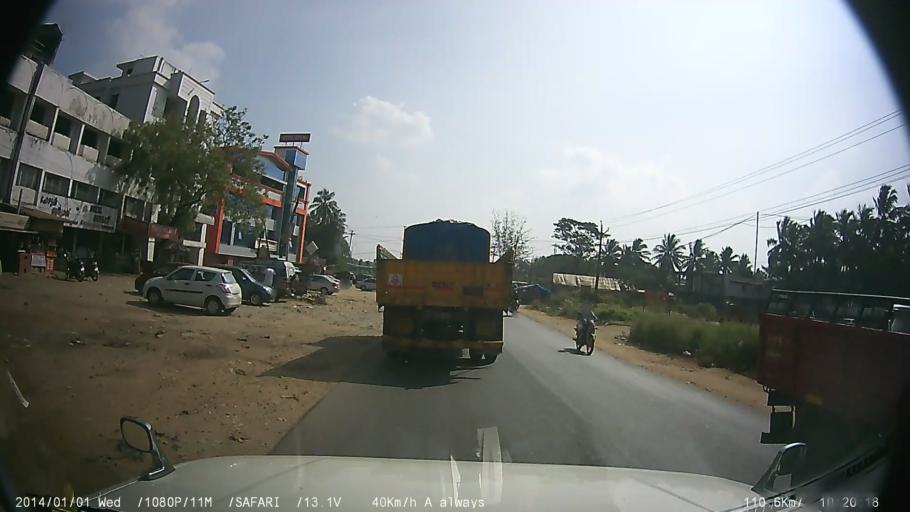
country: IN
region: Kerala
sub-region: Thrissur District
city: Chelakara
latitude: 10.5908
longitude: 76.4731
